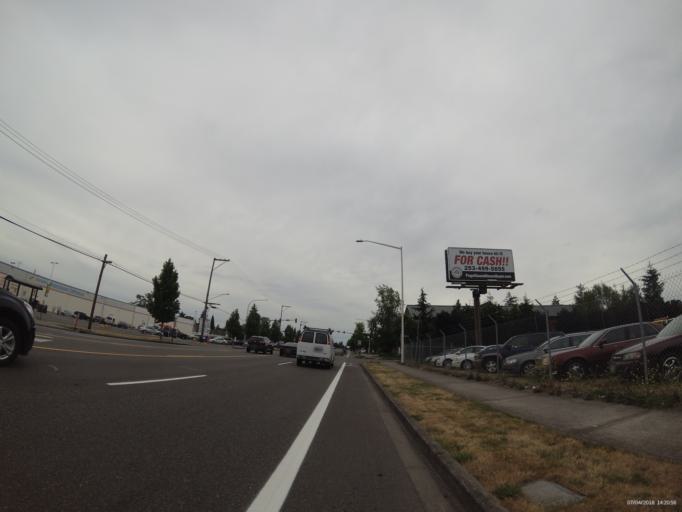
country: US
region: Washington
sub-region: Pierce County
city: McChord Air Force Base
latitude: 47.1583
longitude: -122.4893
